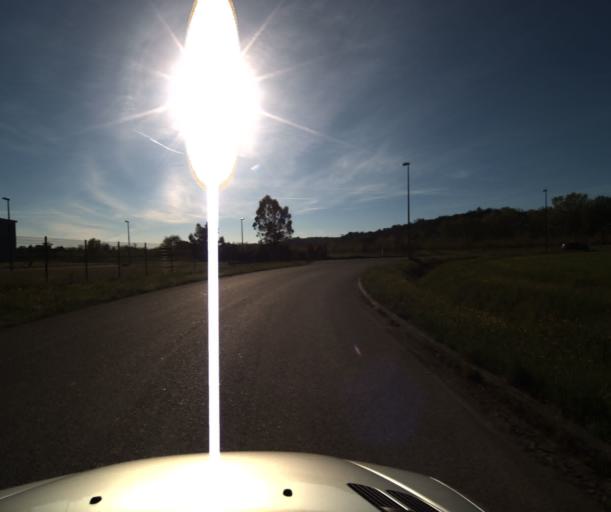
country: FR
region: Midi-Pyrenees
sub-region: Departement du Tarn-et-Garonne
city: Moissac
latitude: 44.1059
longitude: 1.1086
